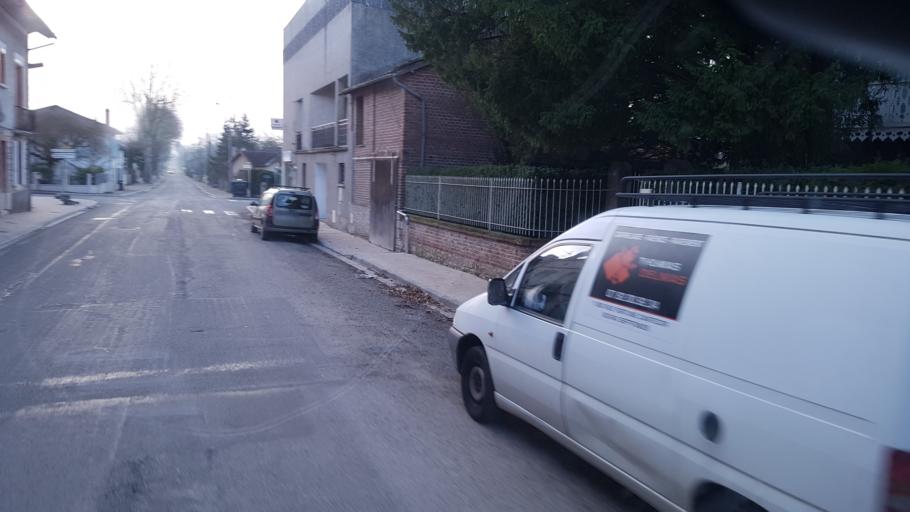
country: FR
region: Midi-Pyrenees
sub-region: Departement du Tarn-et-Garonne
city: Caussade
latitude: 44.1592
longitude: 1.5413
